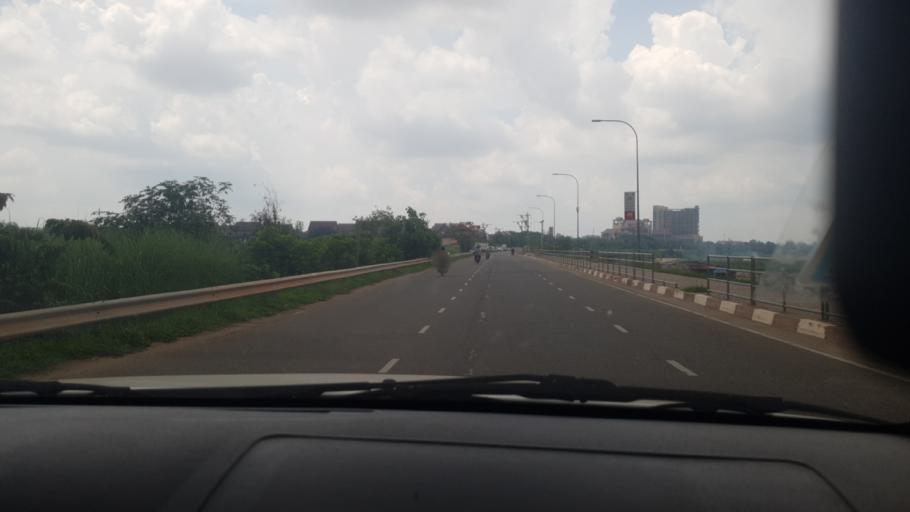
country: LA
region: Vientiane
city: Vientiane
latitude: 17.9540
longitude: 102.6132
